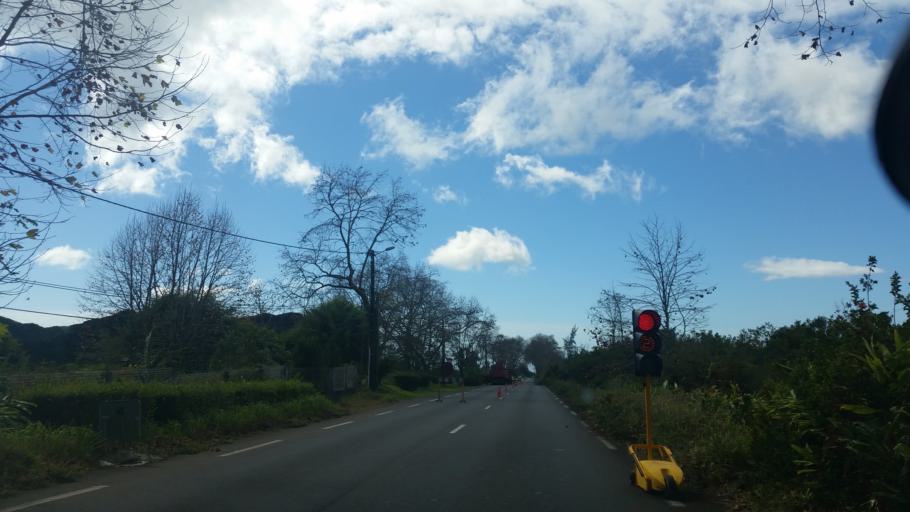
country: RE
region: Reunion
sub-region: Reunion
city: Saint-Benoit
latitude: -21.1203
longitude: 55.6435
